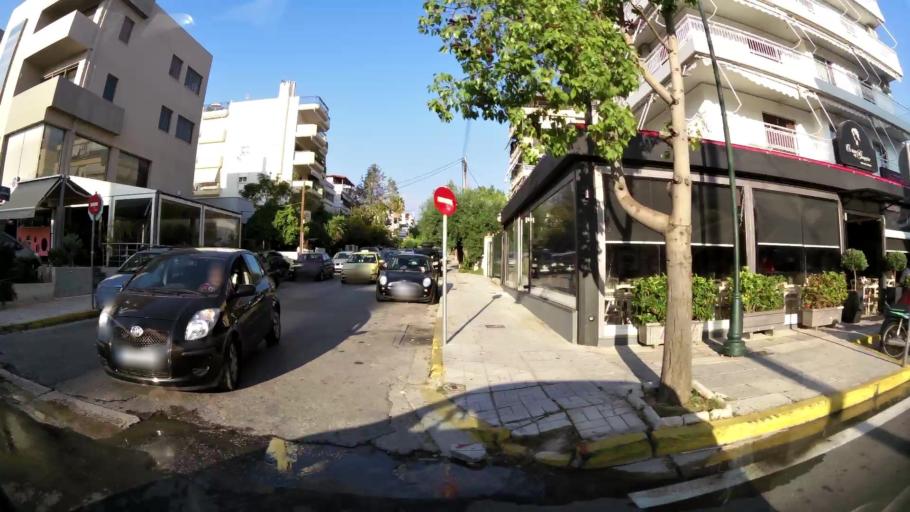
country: GR
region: Attica
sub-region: Nomarchia Athinas
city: Argyroupoli
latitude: 37.8928
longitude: 23.7645
